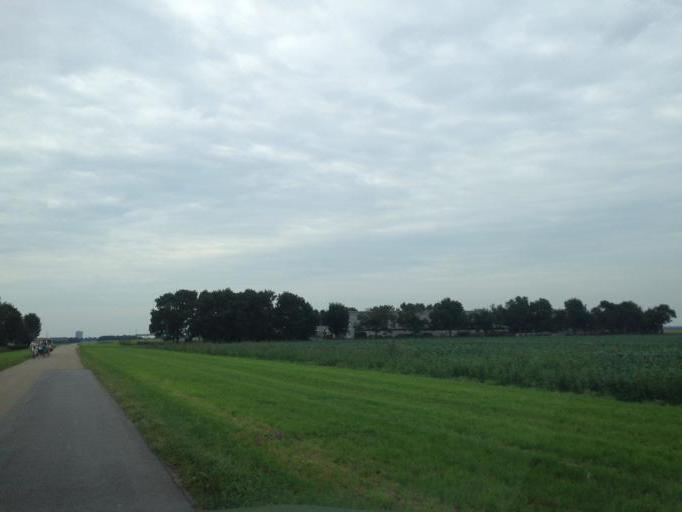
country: NL
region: Utrecht
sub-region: Gemeente Bunschoten
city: Spakenburg
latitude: 52.3722
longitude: 5.3429
